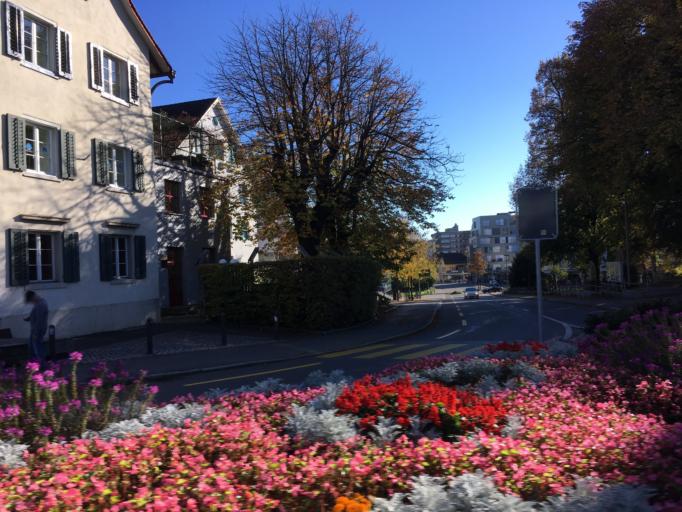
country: CH
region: Zurich
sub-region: Bezirk Hinwil
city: Wetzikon
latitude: 47.3268
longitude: 8.7990
